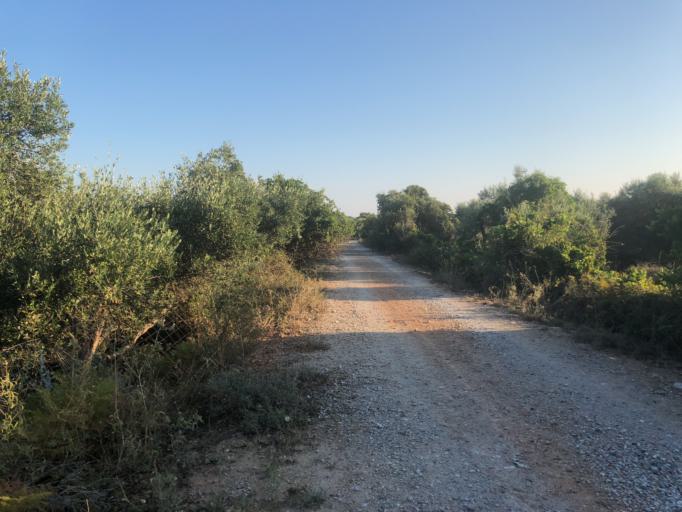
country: GR
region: Crete
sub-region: Nomos Chanias
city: Georgioupolis
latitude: 35.3320
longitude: 24.2927
